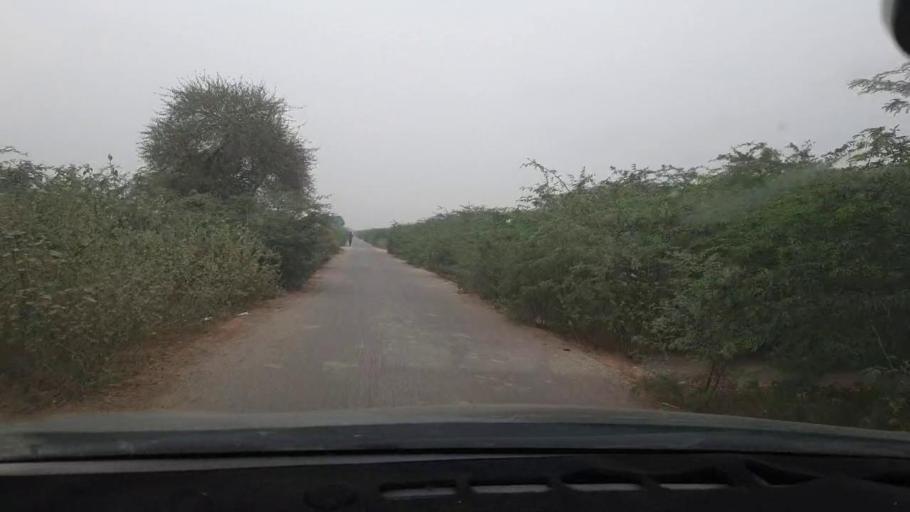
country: PK
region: Sindh
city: Malir Cantonment
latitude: 24.9249
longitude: 67.3315
